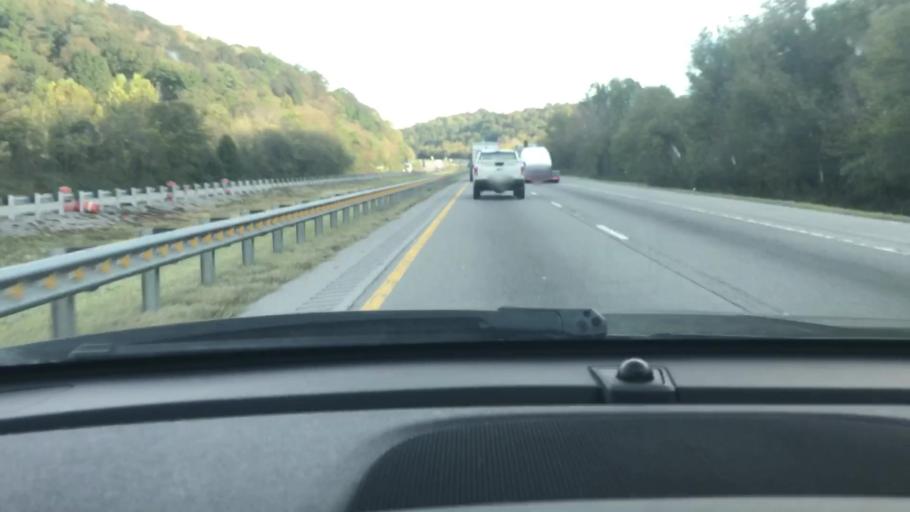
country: US
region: Tennessee
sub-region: Sumner County
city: Millersville
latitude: 36.3926
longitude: -86.7162
